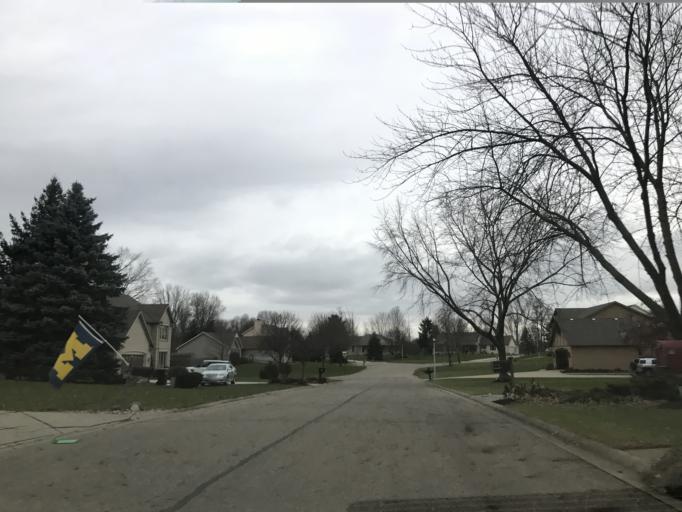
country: US
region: Michigan
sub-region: Eaton County
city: Dimondale
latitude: 42.6561
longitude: -84.6407
